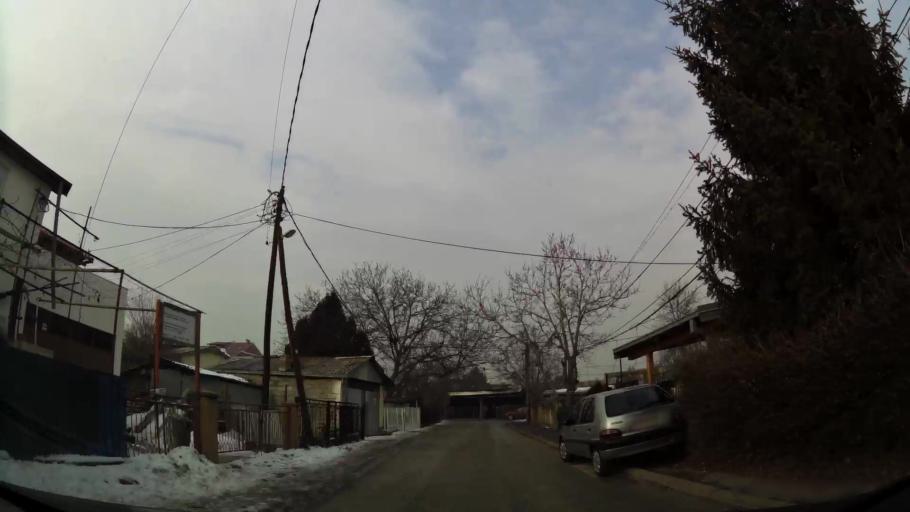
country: MK
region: Kisela Voda
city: Kisela Voda
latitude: 41.9949
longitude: 21.5058
